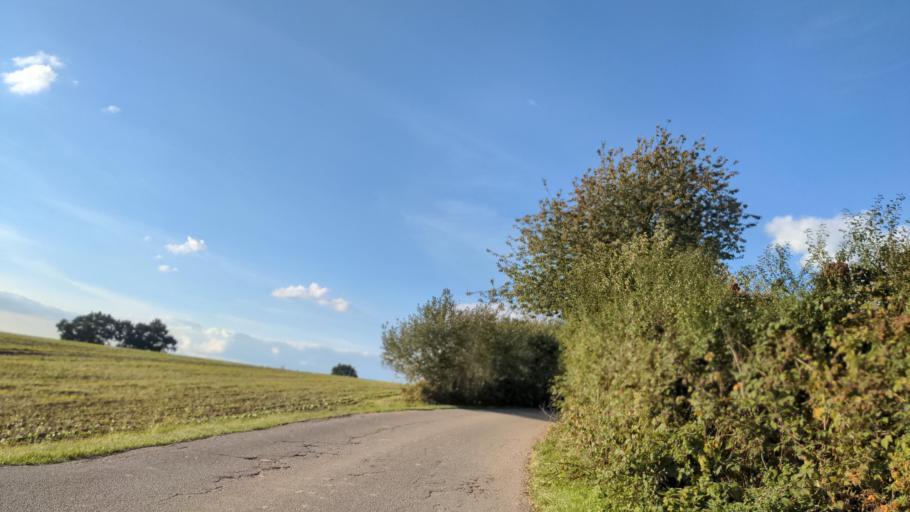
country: DE
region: Schleswig-Holstein
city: Ahrensbok
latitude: 53.9886
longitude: 10.6240
